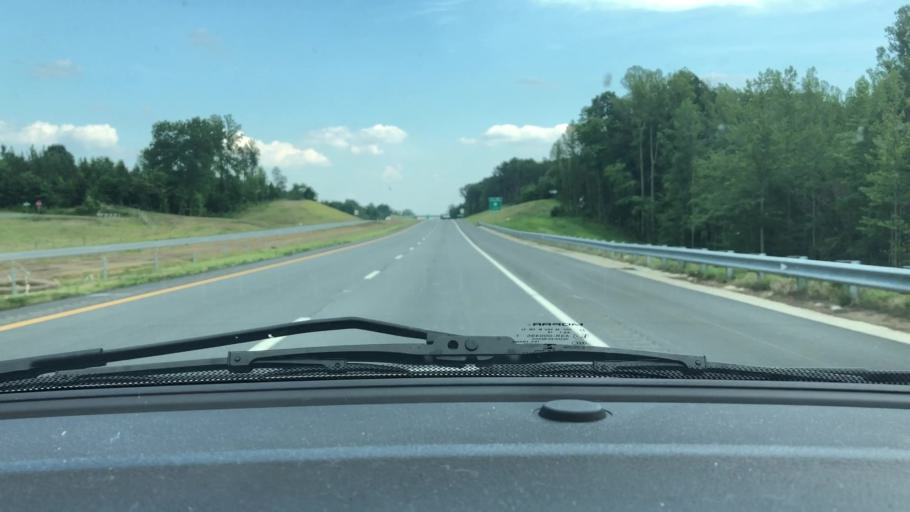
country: US
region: North Carolina
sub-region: Guilford County
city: Stokesdale
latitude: 36.2797
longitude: -79.9377
